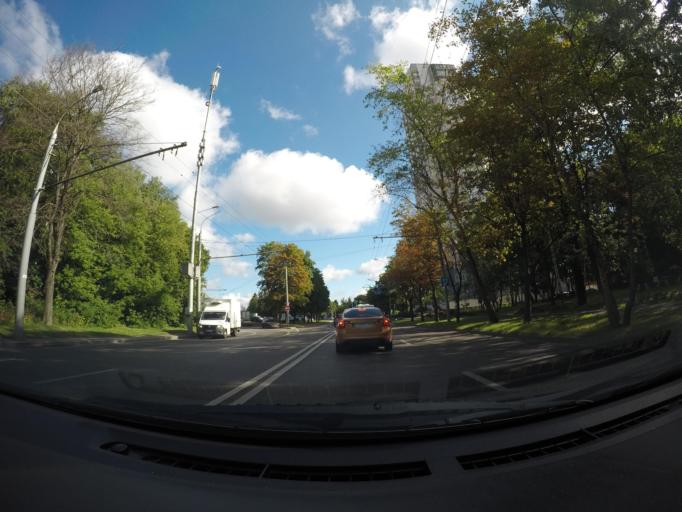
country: RU
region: Moscow
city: Khimki
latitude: 55.8702
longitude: 37.4402
